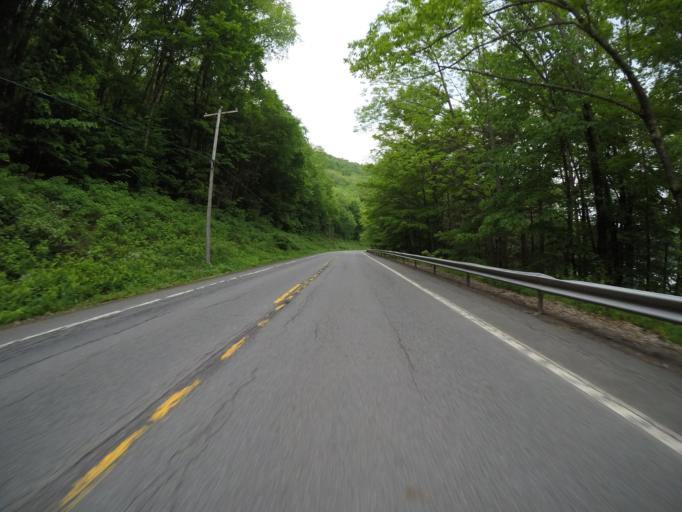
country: US
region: New York
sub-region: Sullivan County
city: Livingston Manor
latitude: 42.0733
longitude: -74.9218
